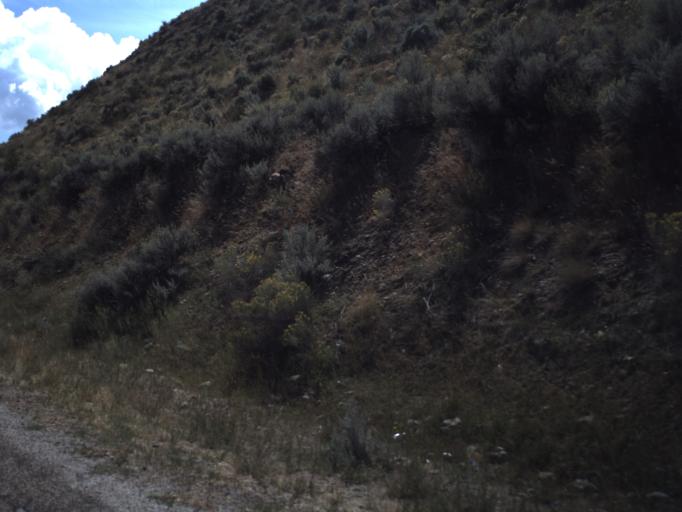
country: US
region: Utah
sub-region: Rich County
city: Randolph
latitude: 41.8489
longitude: -111.3543
